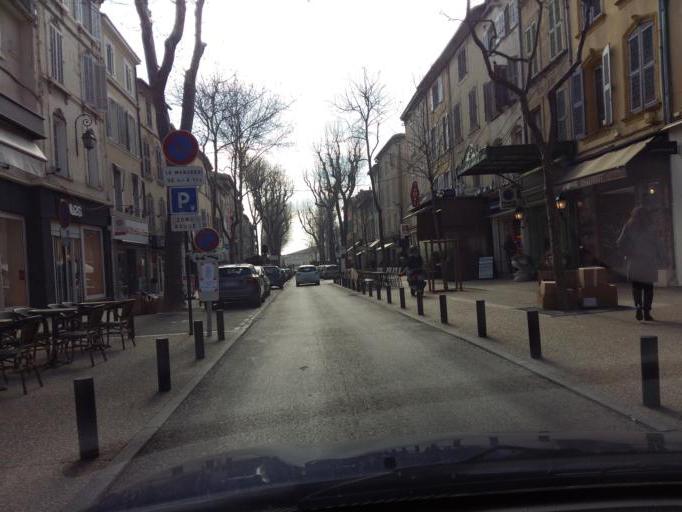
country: FR
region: Provence-Alpes-Cote d'Azur
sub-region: Departement des Bouches-du-Rhone
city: Salon-de-Provence
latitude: 43.6405
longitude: 5.0990
